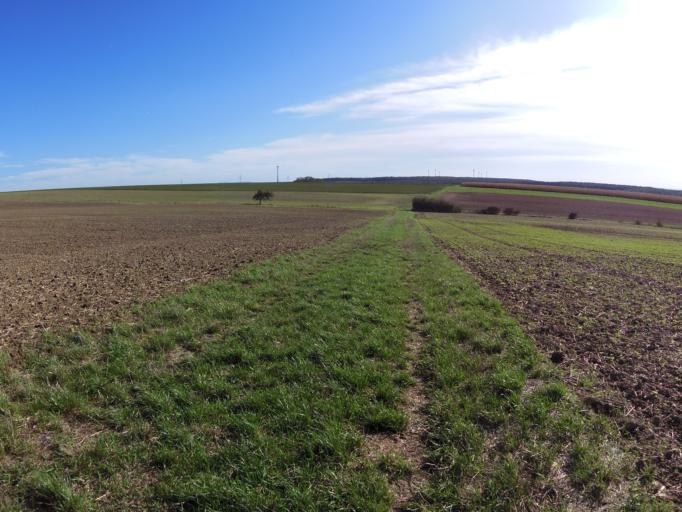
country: DE
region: Bavaria
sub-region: Regierungsbezirk Unterfranken
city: Theilheim
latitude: 49.7671
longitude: 10.0185
